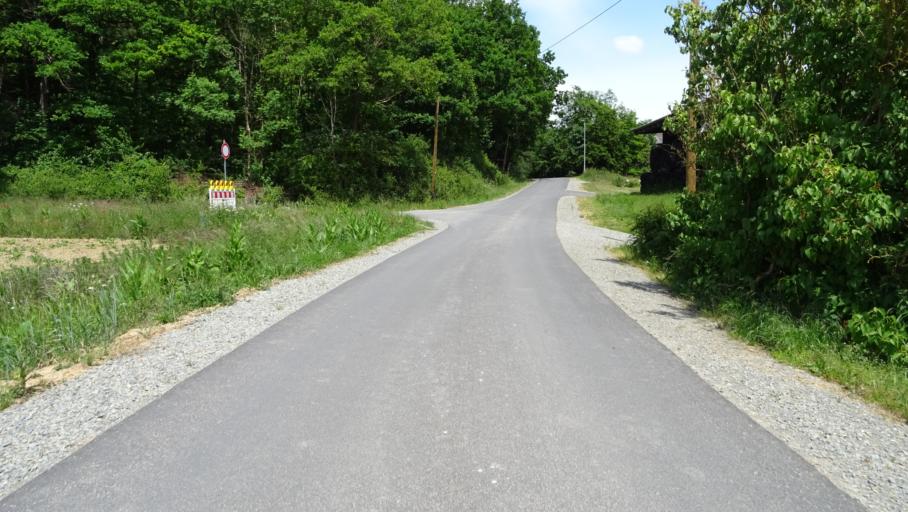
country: DE
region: Baden-Wuerttemberg
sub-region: Karlsruhe Region
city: Buchen
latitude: 49.4882
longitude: 9.3375
